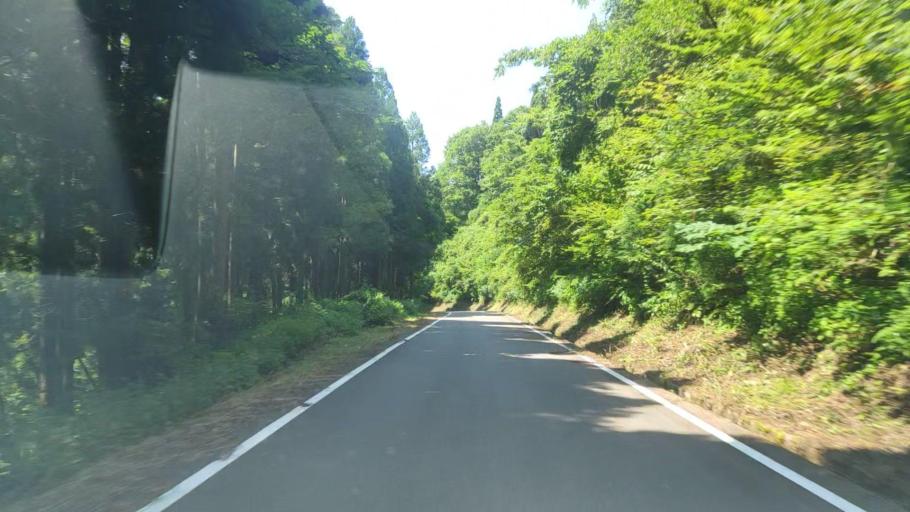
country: JP
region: Fukui
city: Katsuyama
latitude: 36.1283
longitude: 136.5087
